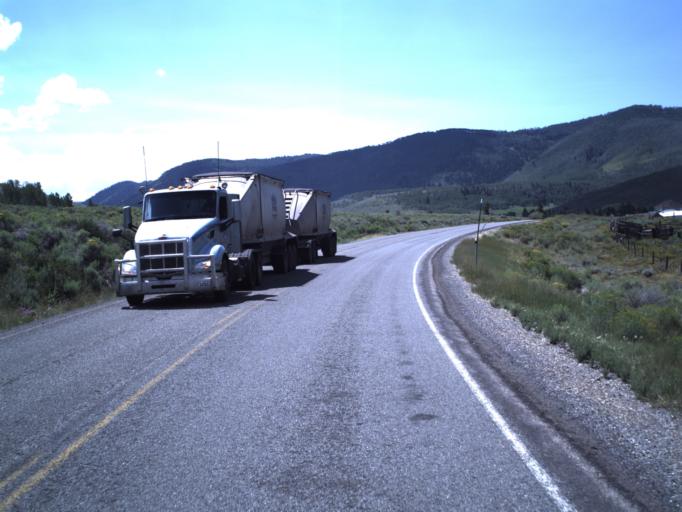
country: US
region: Utah
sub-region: Carbon County
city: Helper
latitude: 39.7329
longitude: -111.1545
